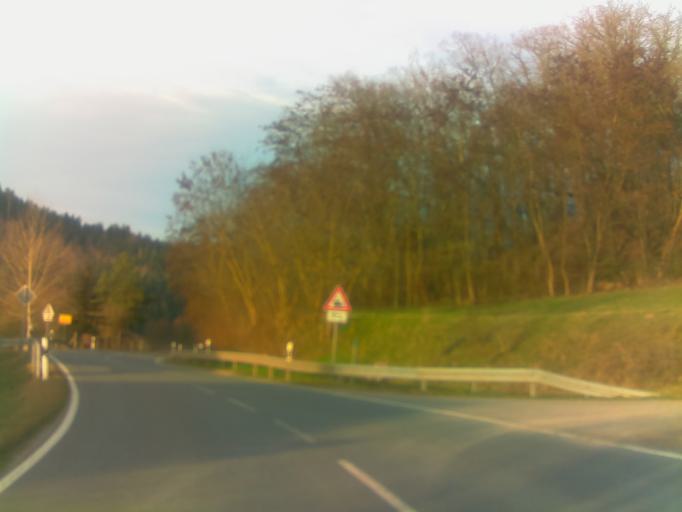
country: DE
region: Thuringia
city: Langenorla
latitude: 50.7440
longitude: 11.5729
